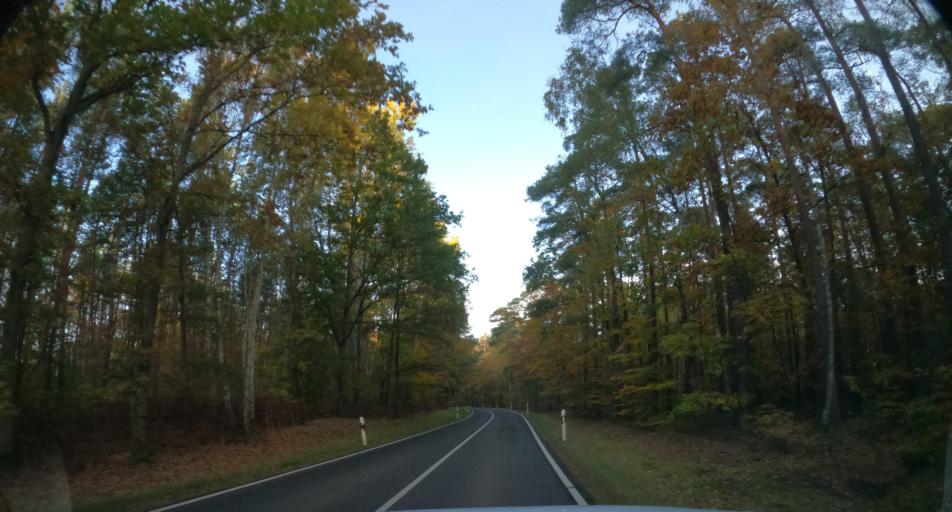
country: DE
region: Mecklenburg-Vorpommern
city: Ahlbeck
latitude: 53.6523
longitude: 14.1887
